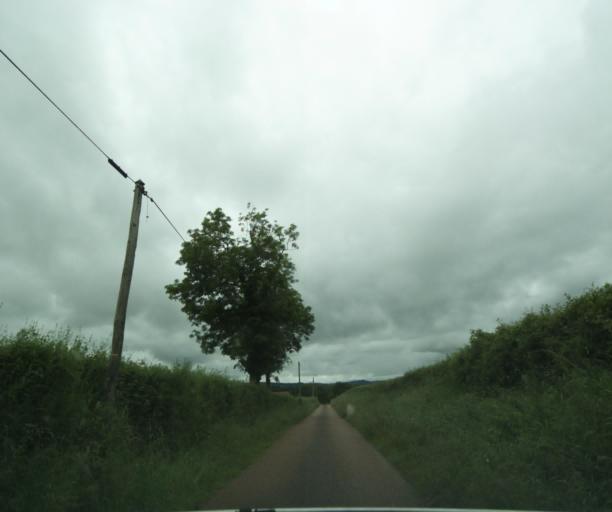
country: FR
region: Bourgogne
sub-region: Departement de Saone-et-Loire
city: Charolles
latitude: 46.4729
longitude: 4.3510
